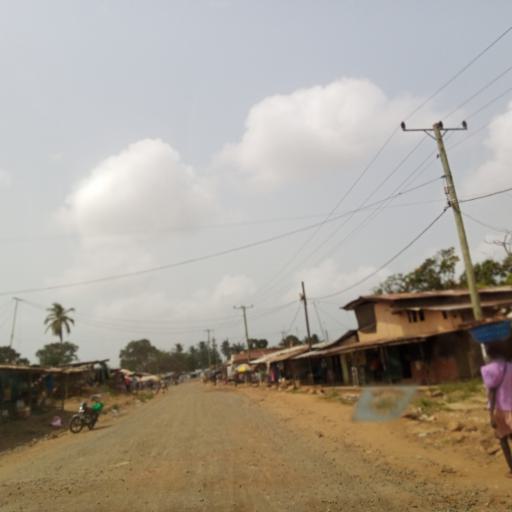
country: LR
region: Montserrado
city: Monrovia
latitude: 6.3476
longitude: -10.7323
